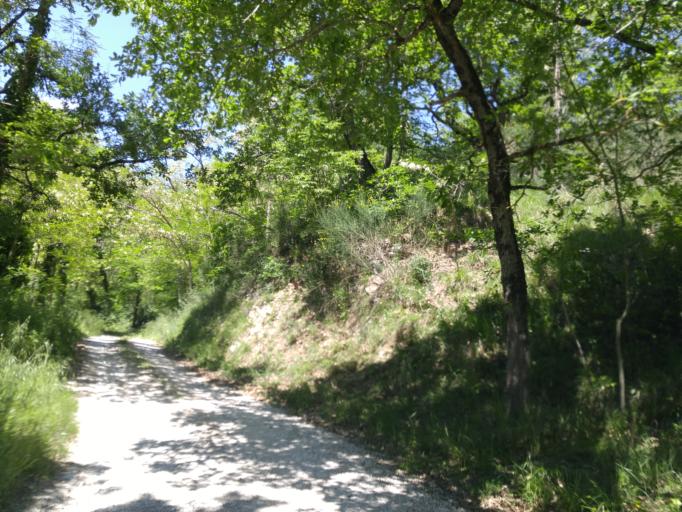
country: IT
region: The Marches
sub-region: Provincia di Pesaro e Urbino
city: Canavaccio
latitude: 43.7154
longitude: 12.6887
